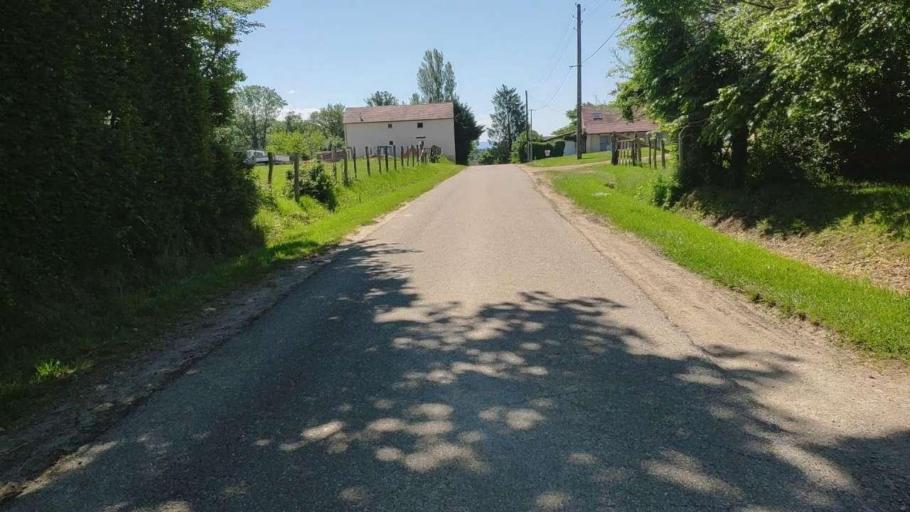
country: FR
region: Franche-Comte
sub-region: Departement du Jura
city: Bletterans
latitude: 46.7653
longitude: 5.4107
